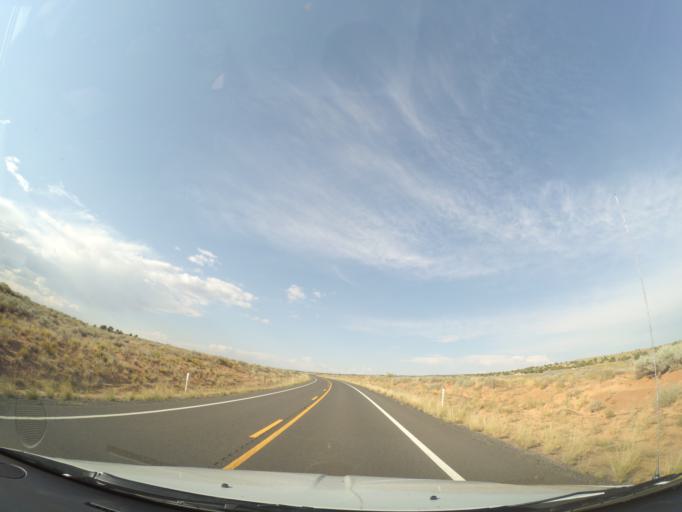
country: US
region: Arizona
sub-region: Coconino County
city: Kaibito
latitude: 36.4909
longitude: -111.4109
